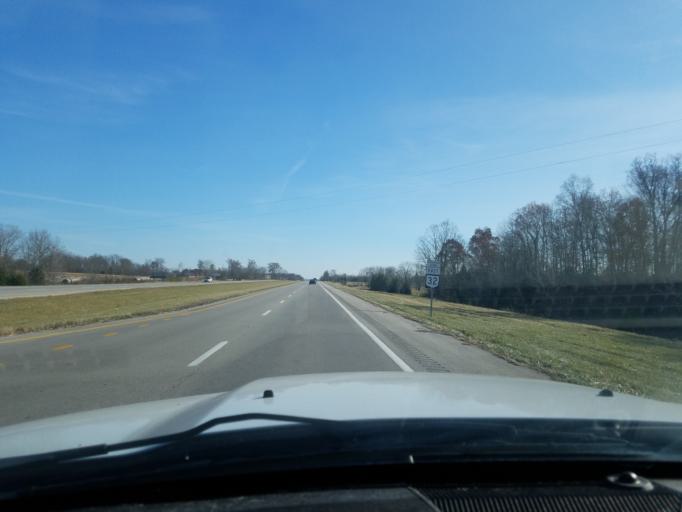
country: US
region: Ohio
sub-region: Adams County
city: Winchester
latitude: 38.9330
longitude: -83.5964
